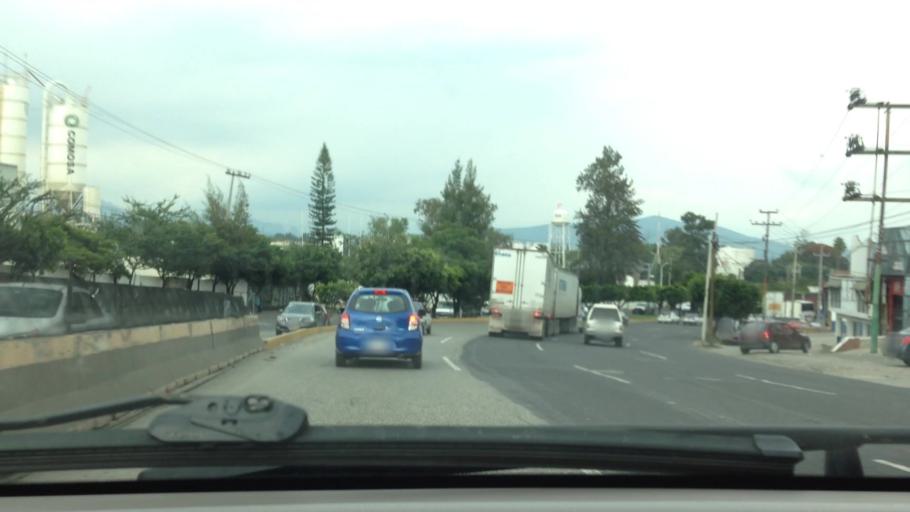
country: MX
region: Morelos
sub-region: Tepoztlan
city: Loma Bonita
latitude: 18.9198
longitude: -99.1948
